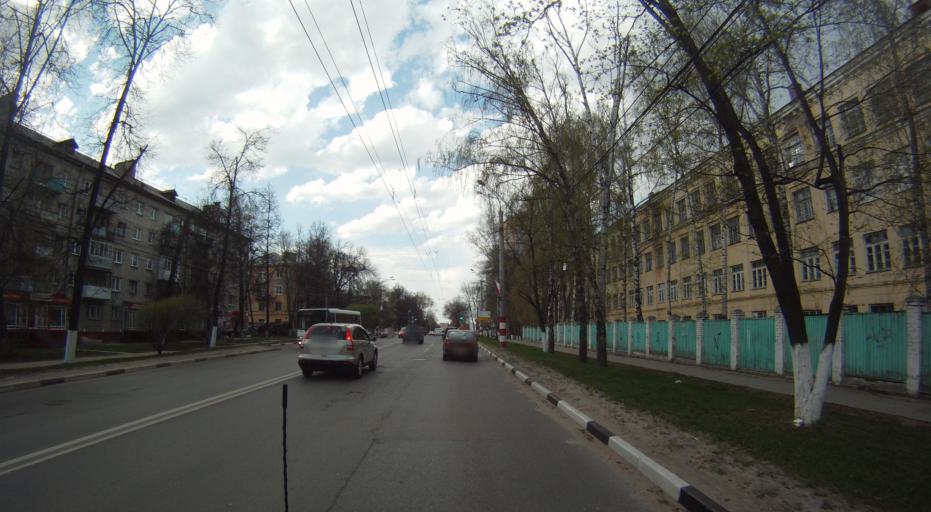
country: RU
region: Nizjnij Novgorod
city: Nizhniy Novgorod
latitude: 56.3121
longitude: 44.0199
